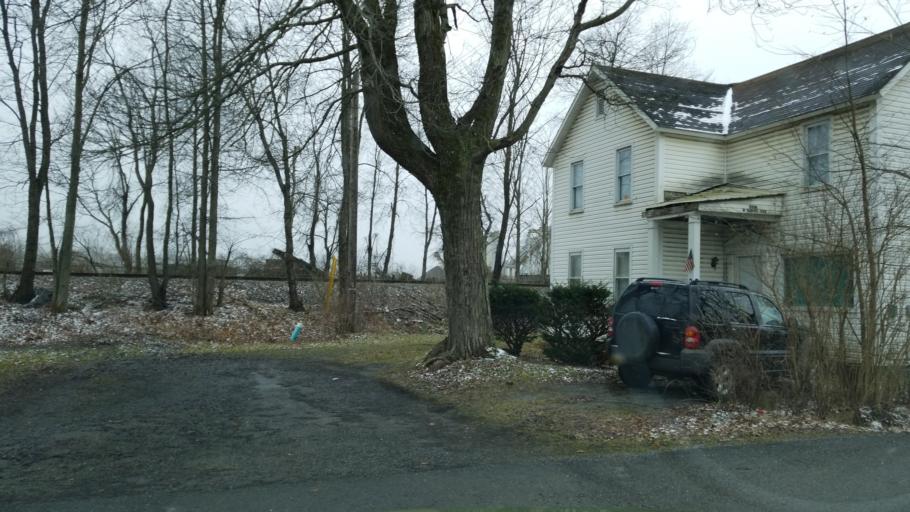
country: US
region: Pennsylvania
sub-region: Clearfield County
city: DuBois
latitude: 41.1280
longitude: -78.7602
